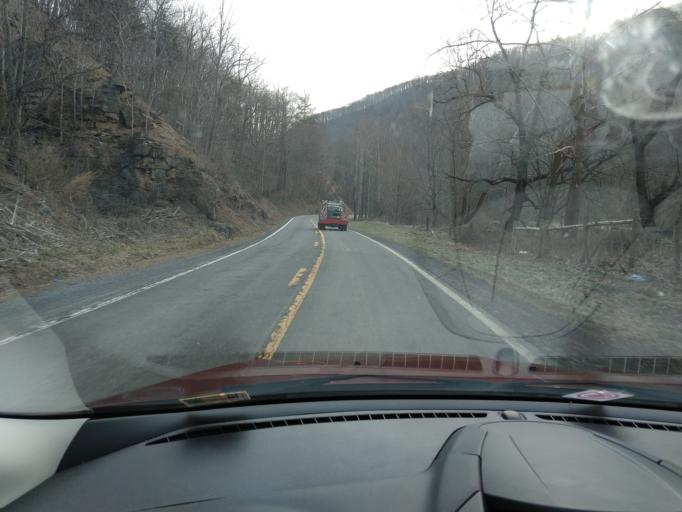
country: US
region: West Virginia
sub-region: Pendleton County
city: Franklin
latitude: 38.5912
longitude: -79.3979
